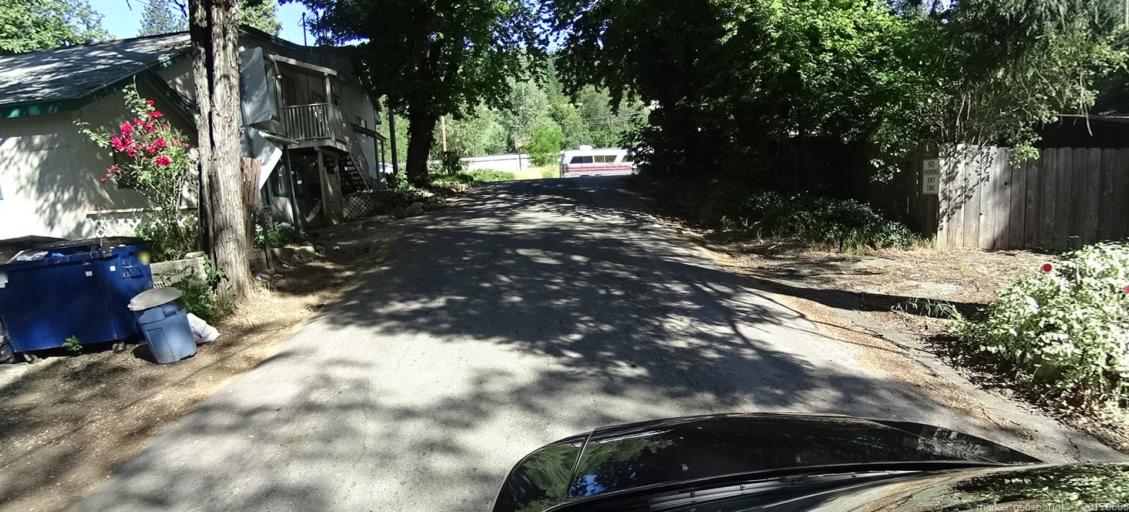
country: US
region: California
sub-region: Siskiyou County
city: Dunsmuir
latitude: 41.1958
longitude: -122.2807
